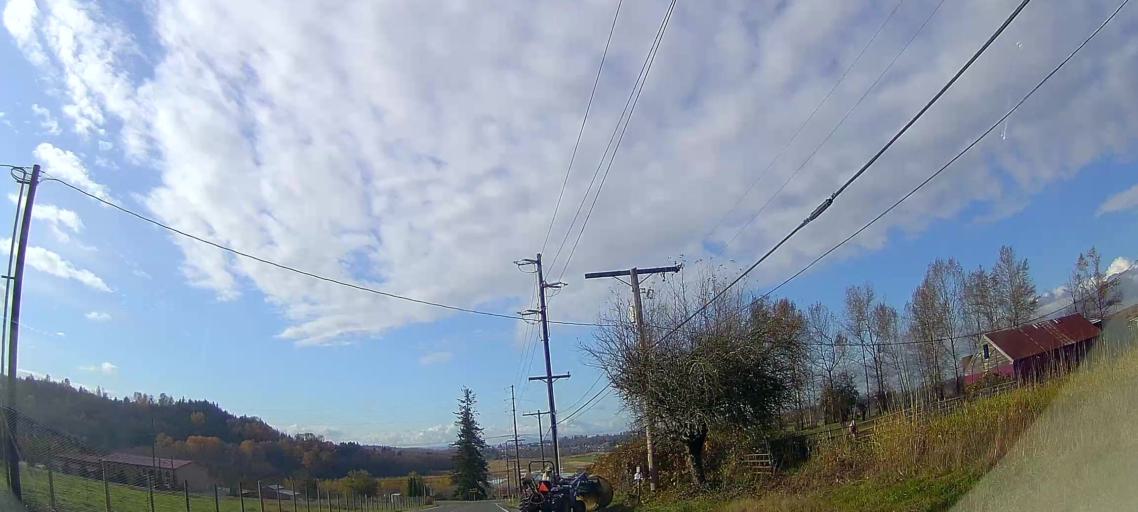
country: US
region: Washington
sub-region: Skagit County
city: Big Lake
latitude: 48.4354
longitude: -122.2624
